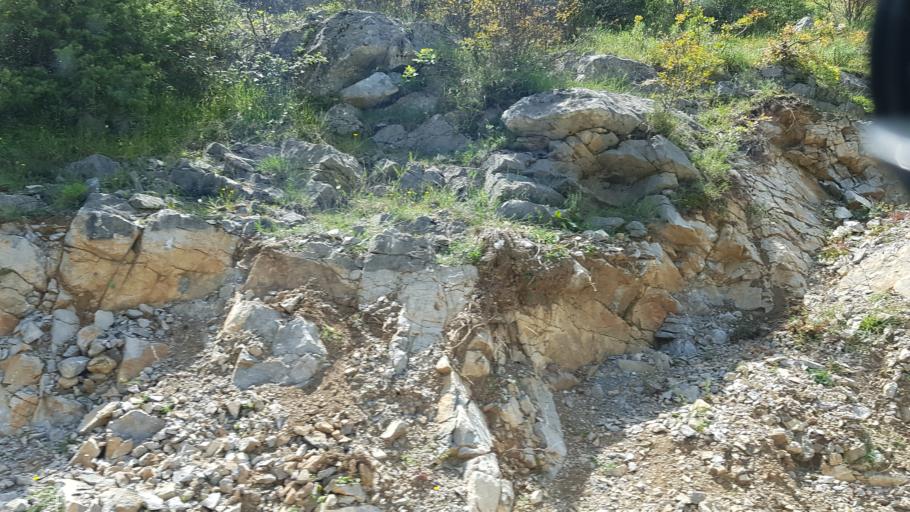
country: AL
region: Shkoder
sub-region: Rrethi i Shkodres
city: Guri i Zi
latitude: 42.1222
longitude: 19.6052
